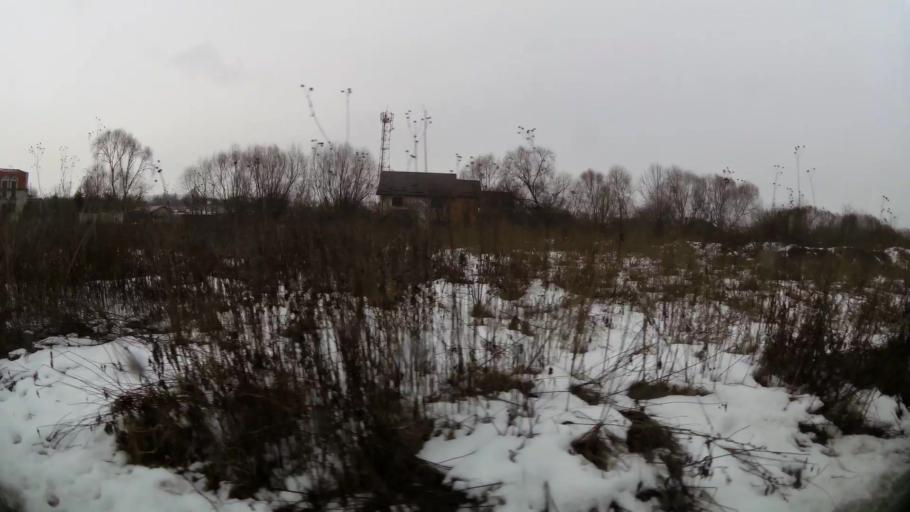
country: RO
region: Ilfov
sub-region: Comuna Mogosoaia
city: Mogosoaia
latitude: 44.5138
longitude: 26.0264
